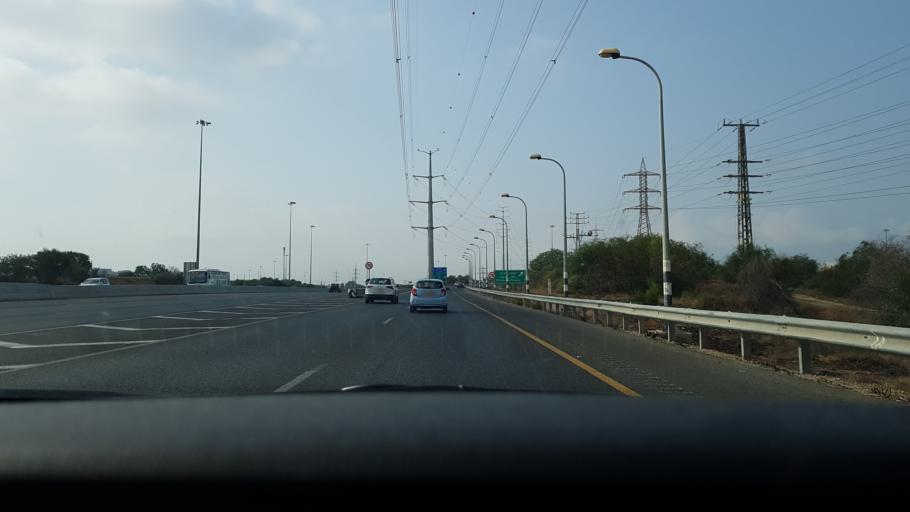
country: IL
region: Central District
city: Rishon LeZiyyon
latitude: 31.9675
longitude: 34.7874
